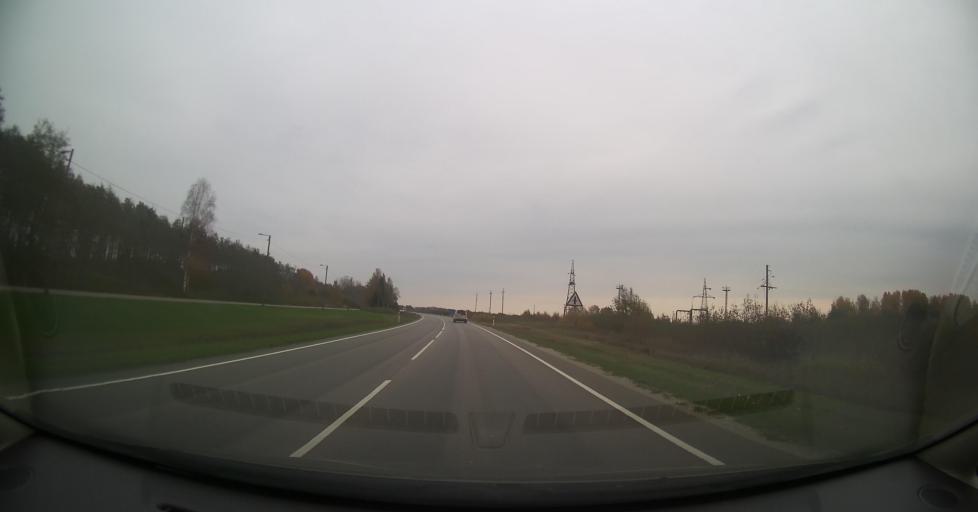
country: EE
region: Laeaene
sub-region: Ridala Parish
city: Uuemoisa
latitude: 58.9564
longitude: 23.7528
